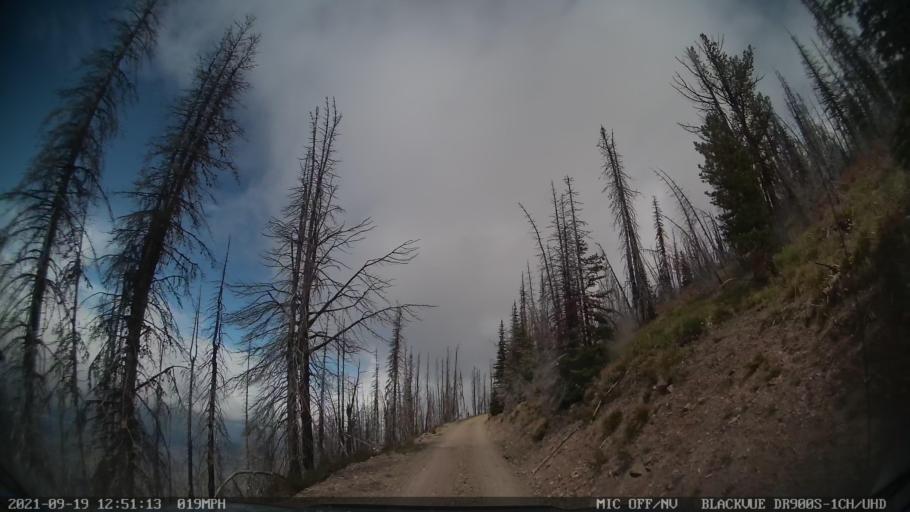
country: US
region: Montana
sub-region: Missoula County
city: Seeley Lake
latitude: 47.1885
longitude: -113.3596
